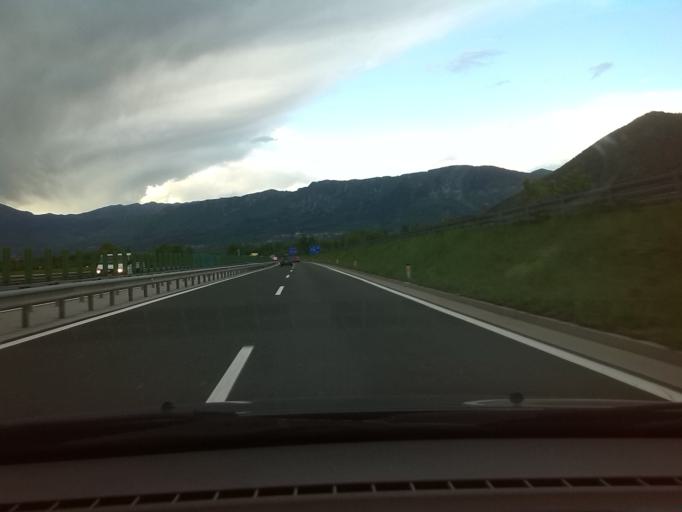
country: SI
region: Vipava
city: Vipava
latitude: 45.8215
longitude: 13.9613
